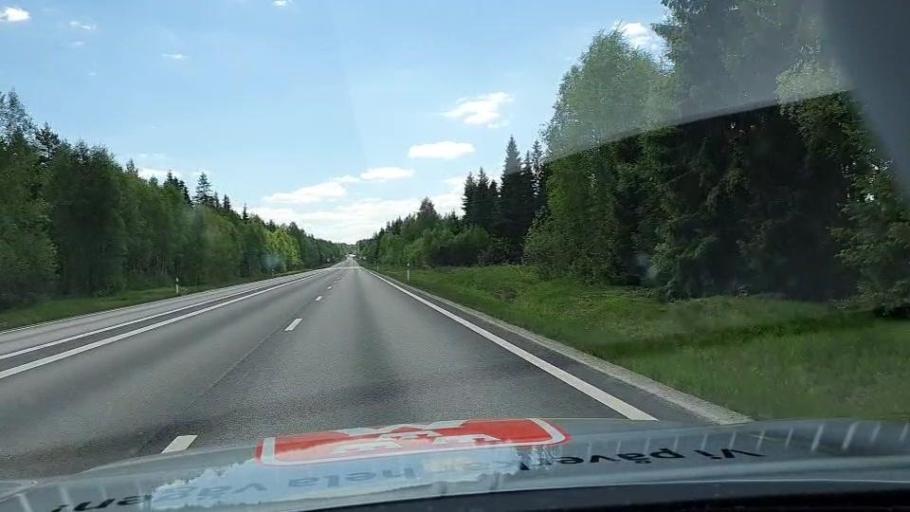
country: SE
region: Kronoberg
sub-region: Vaxjo Kommun
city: Lammhult
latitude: 57.1022
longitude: 14.6374
